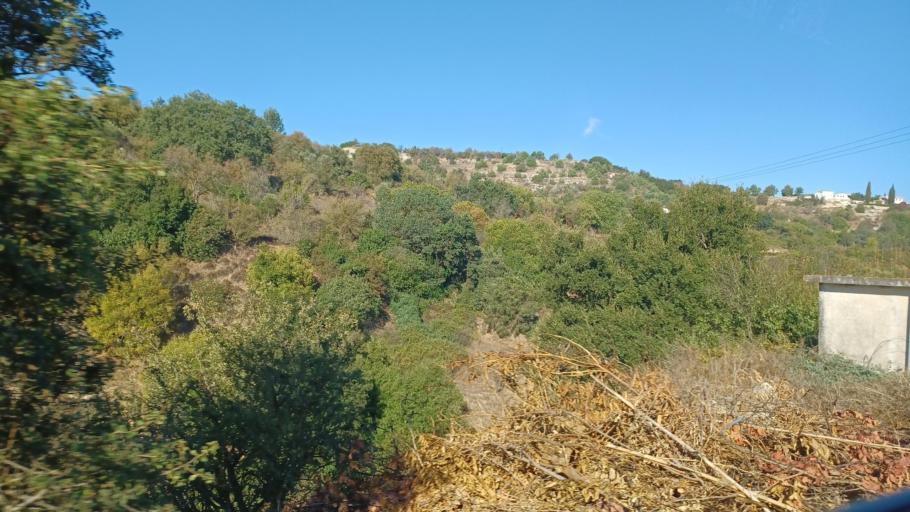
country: CY
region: Pafos
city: Mesogi
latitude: 34.8508
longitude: 32.5181
